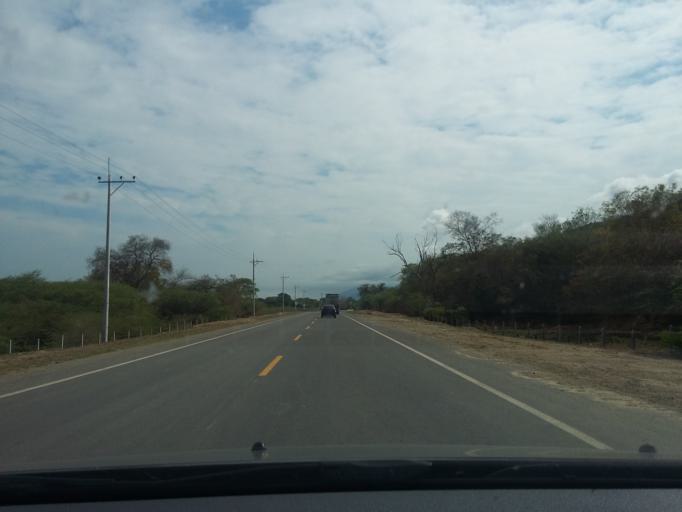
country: CO
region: Tolima
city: Ambalema
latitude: 4.7698
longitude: -74.7657
